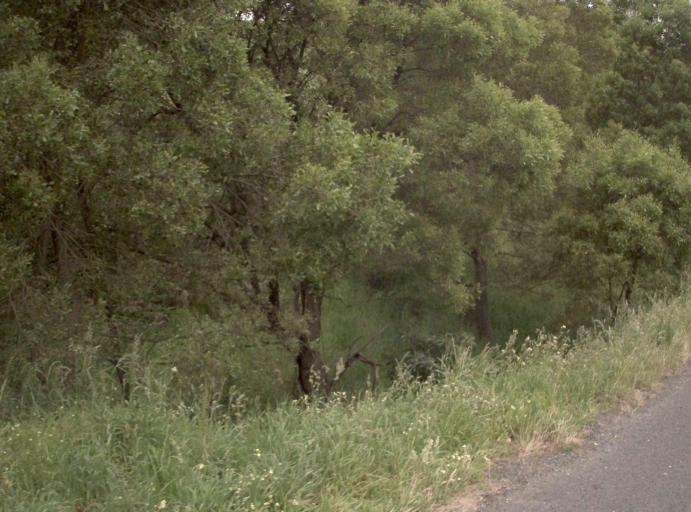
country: AU
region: Victoria
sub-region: Bass Coast
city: North Wonthaggi
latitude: -38.4234
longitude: 145.7966
